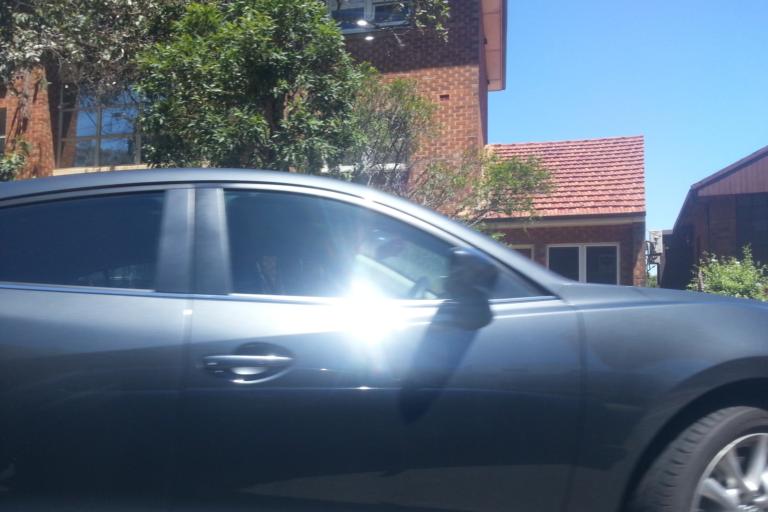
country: AU
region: New South Wales
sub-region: Wollongong
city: Gwynneville
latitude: -34.4253
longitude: 150.8843
